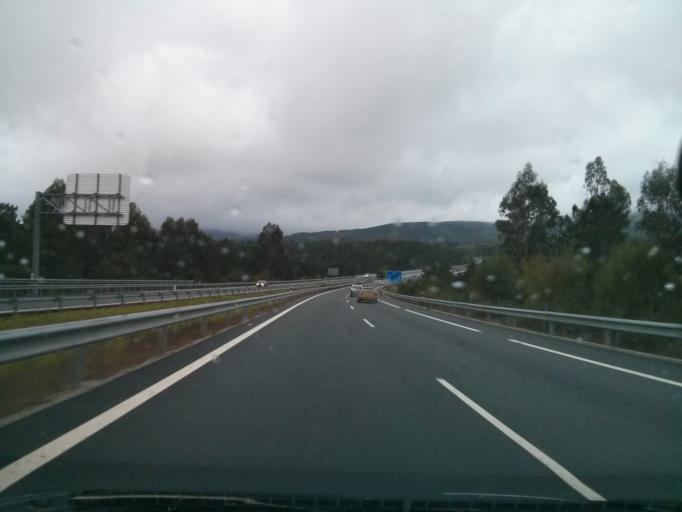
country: ES
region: Galicia
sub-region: Provincia de Pontevedra
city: Covelo
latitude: 42.2017
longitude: -8.2816
